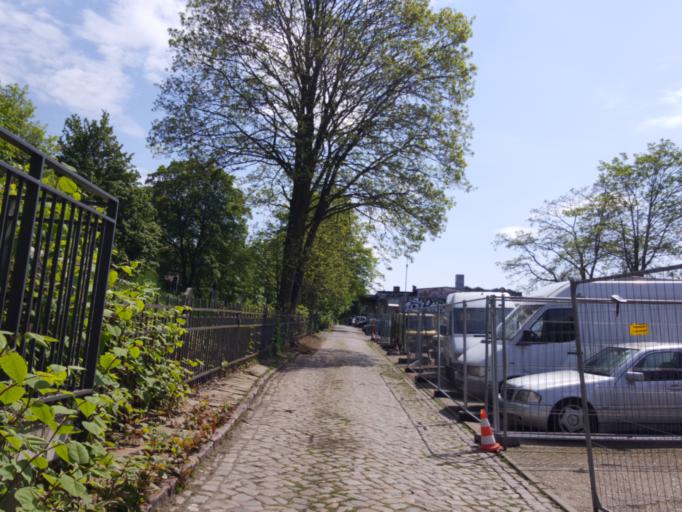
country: DE
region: Hamburg
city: Borgfelde
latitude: 53.5632
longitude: 10.0277
